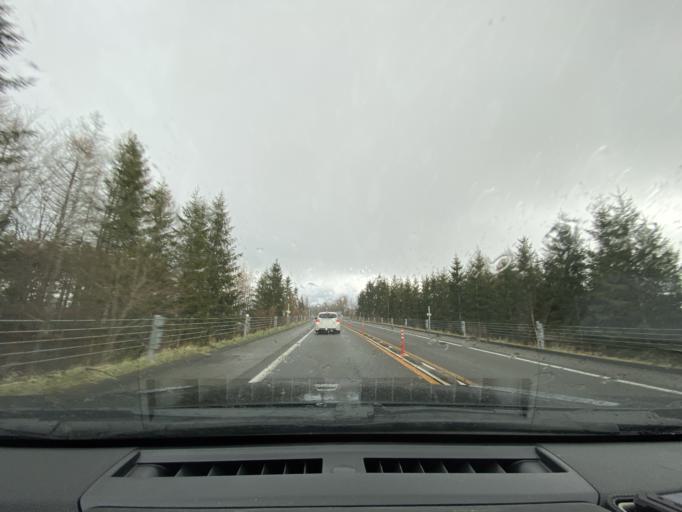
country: JP
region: Hokkaido
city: Otofuke
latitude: 42.9721
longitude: 142.8847
